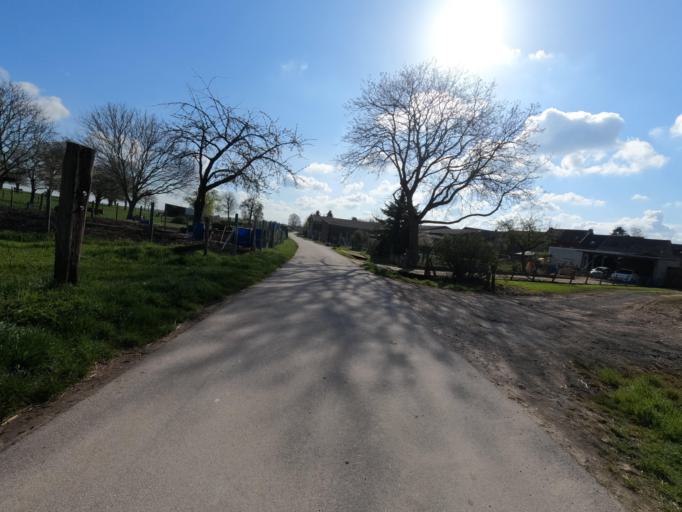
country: DE
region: North Rhine-Westphalia
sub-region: Regierungsbezirk Koln
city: Linnich
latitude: 51.0031
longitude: 6.3454
